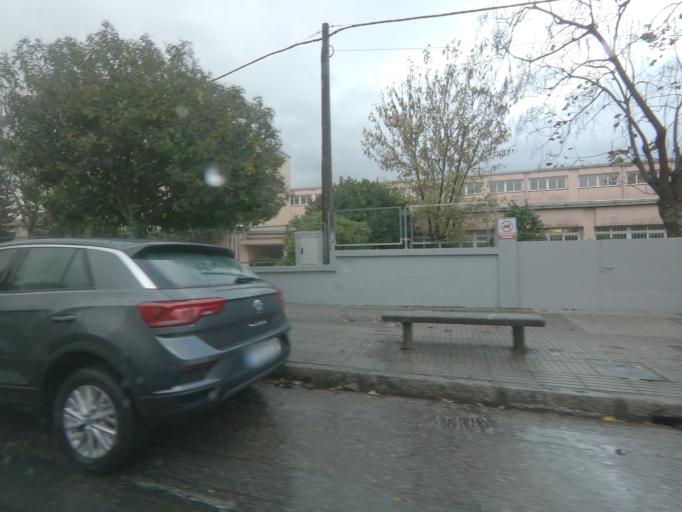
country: ES
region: Galicia
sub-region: Provincia de Pontevedra
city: Pontevedra
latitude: 42.4380
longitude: -8.6396
